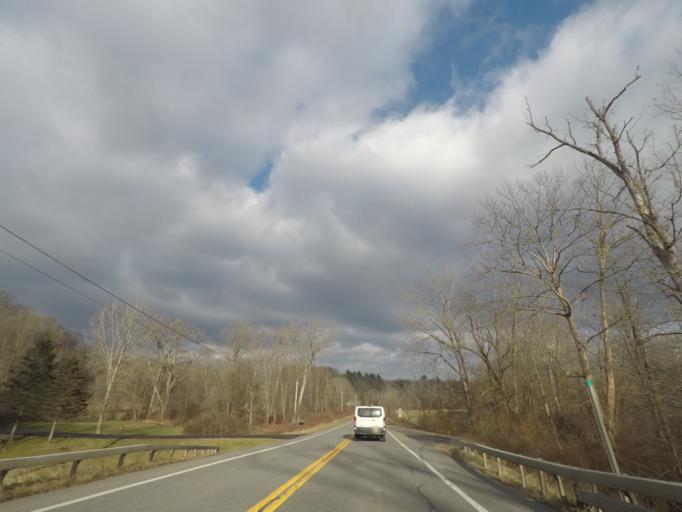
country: US
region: New York
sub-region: Albany County
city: Voorheesville
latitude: 42.6672
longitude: -73.8963
